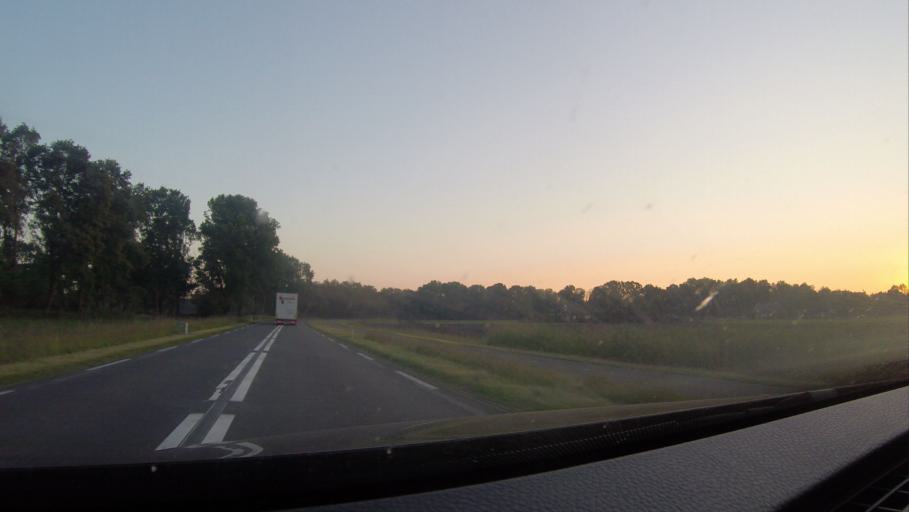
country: NL
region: Overijssel
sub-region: Gemeente Raalte
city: Raalte
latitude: 52.3496
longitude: 6.2732
